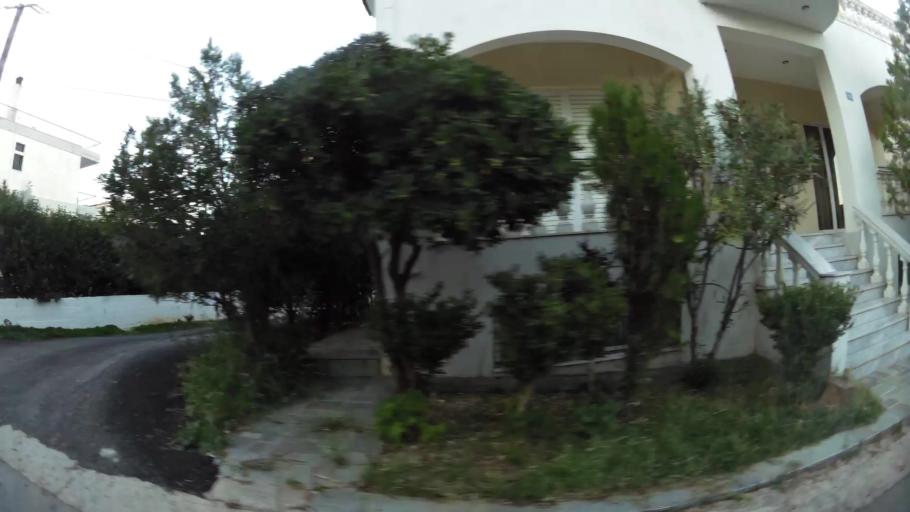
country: GR
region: Attica
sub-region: Nomarchia Anatolikis Attikis
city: Paiania
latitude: 37.9541
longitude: 23.8468
